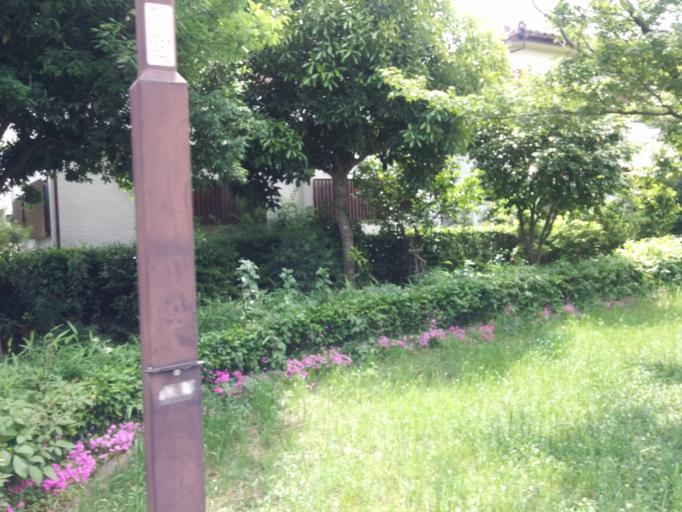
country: JP
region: Tokyo
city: Higashimurayama-shi
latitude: 35.7605
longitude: 139.4836
